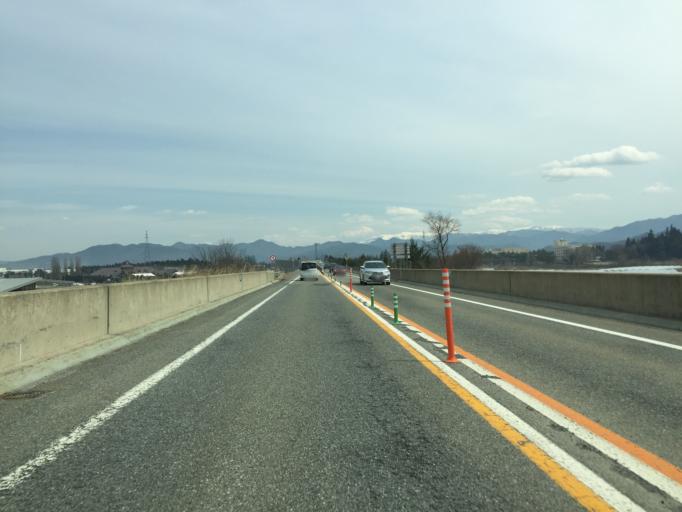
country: JP
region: Yamagata
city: Takahata
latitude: 37.9810
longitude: 140.1470
